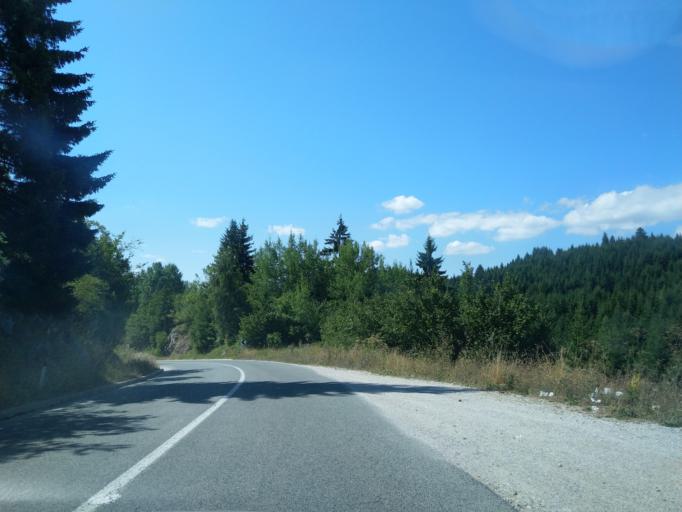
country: RS
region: Central Serbia
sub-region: Zlatiborski Okrug
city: Nova Varos
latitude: 43.4040
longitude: 19.8437
